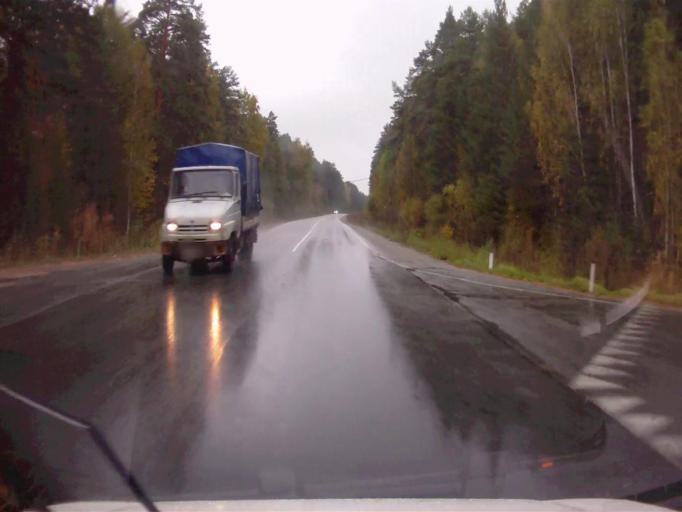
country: RU
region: Chelyabinsk
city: Kyshtym
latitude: 55.6362
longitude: 60.5964
